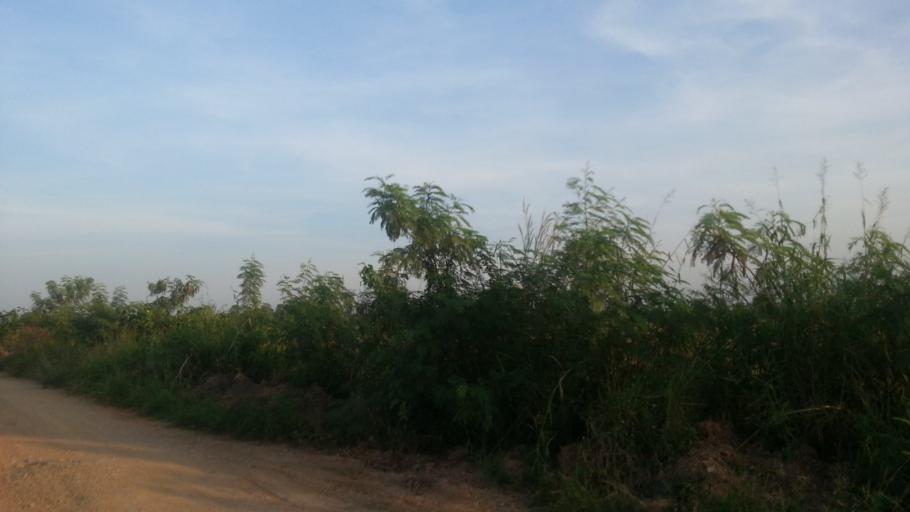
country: TH
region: Pathum Thani
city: Ban Lam Luk Ka
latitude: 14.0352
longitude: 100.8527
